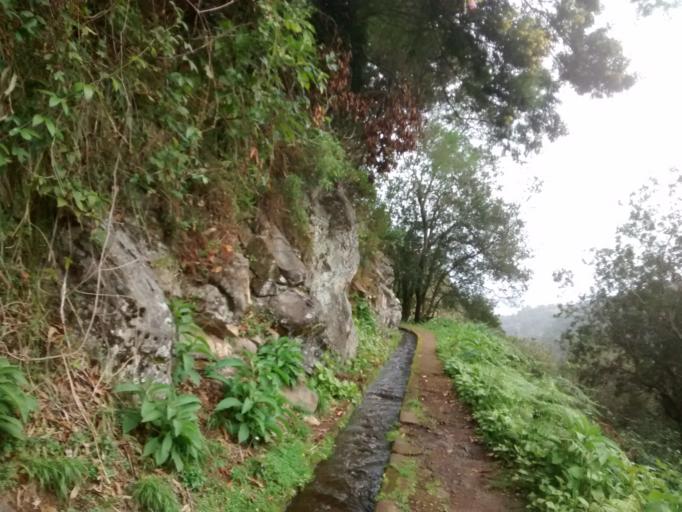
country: PT
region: Madeira
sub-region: Santana
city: Santana
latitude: 32.8092
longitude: -16.9346
